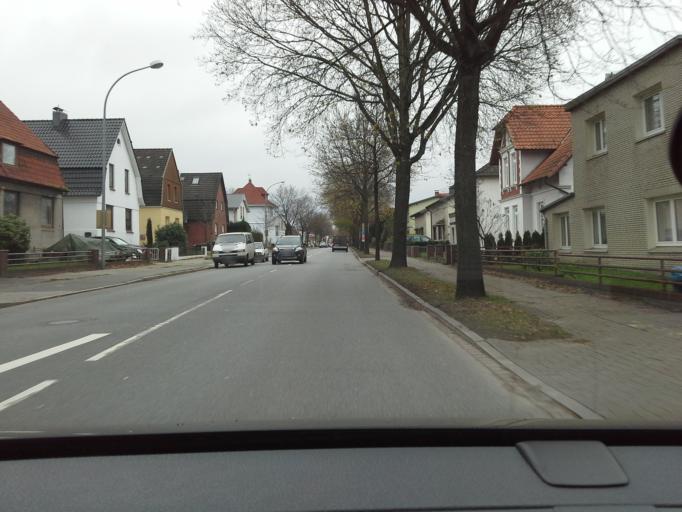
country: DE
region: Schleswig-Holstein
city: Pinneberg
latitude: 53.6724
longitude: 9.7941
